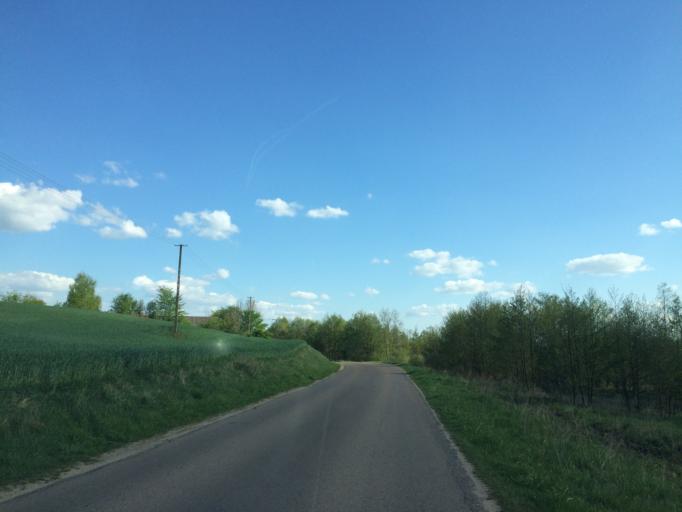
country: PL
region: Warmian-Masurian Voivodeship
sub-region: Powiat dzialdowski
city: Rybno
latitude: 53.4223
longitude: 19.9245
